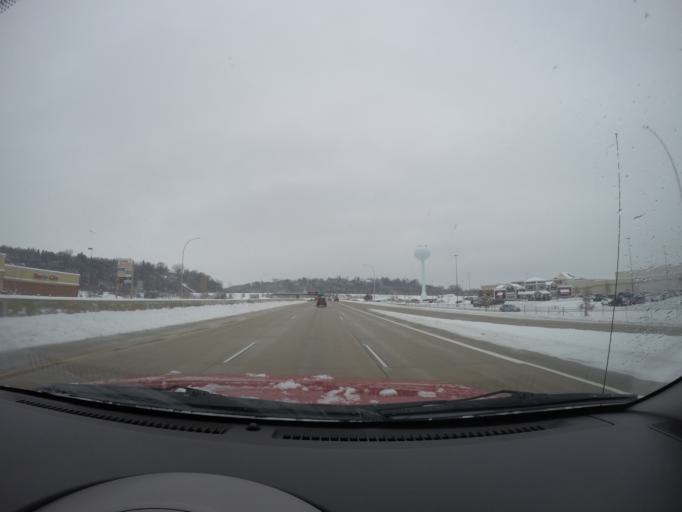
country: US
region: Minnesota
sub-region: Olmsted County
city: Rochester
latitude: 44.0042
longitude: -92.4827
